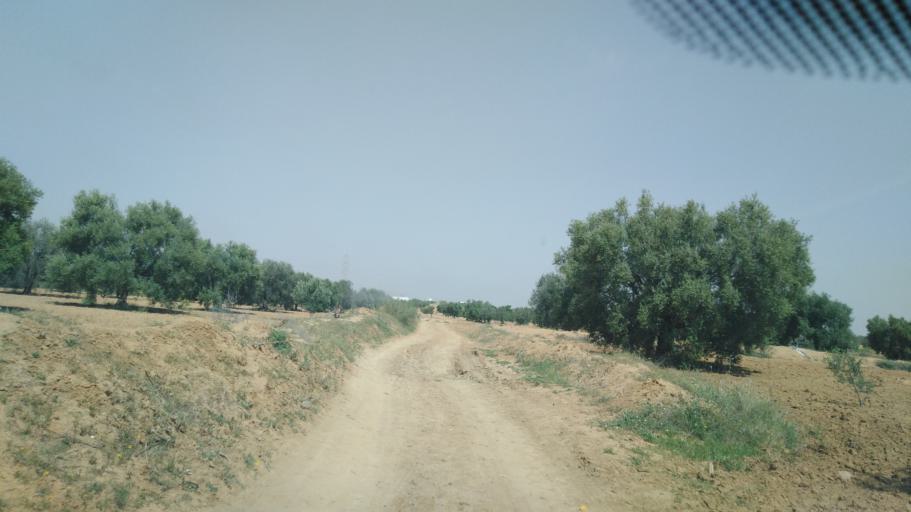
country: TN
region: Safaqis
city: Sfax
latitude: 34.7360
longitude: 10.5740
